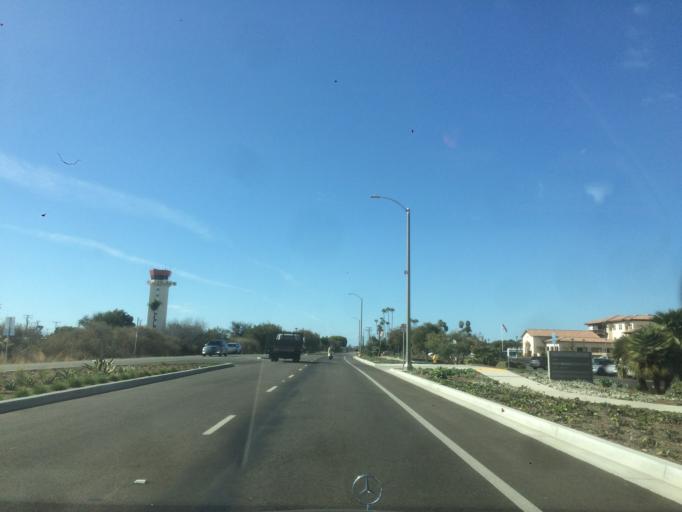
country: US
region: California
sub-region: Santa Barbara County
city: Goleta
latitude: 34.4327
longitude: -119.8421
